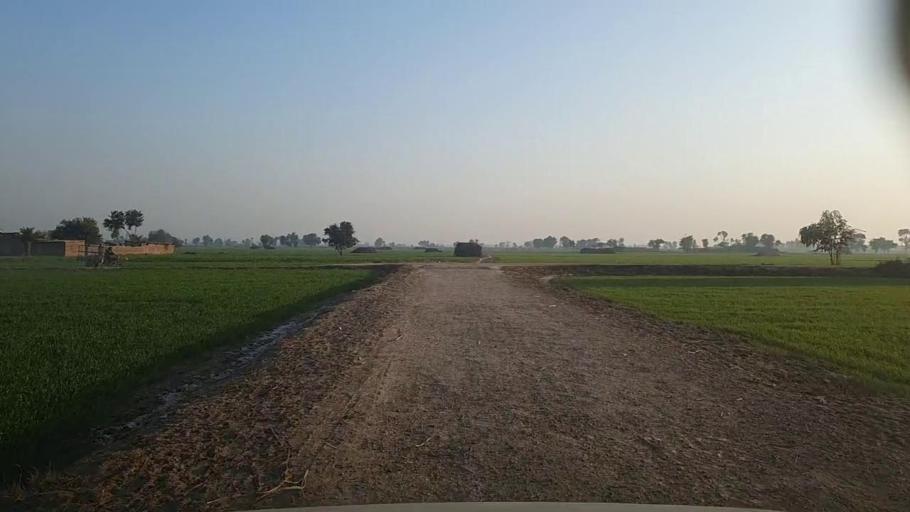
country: PK
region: Sindh
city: Khairpur
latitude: 28.0550
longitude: 69.7589
